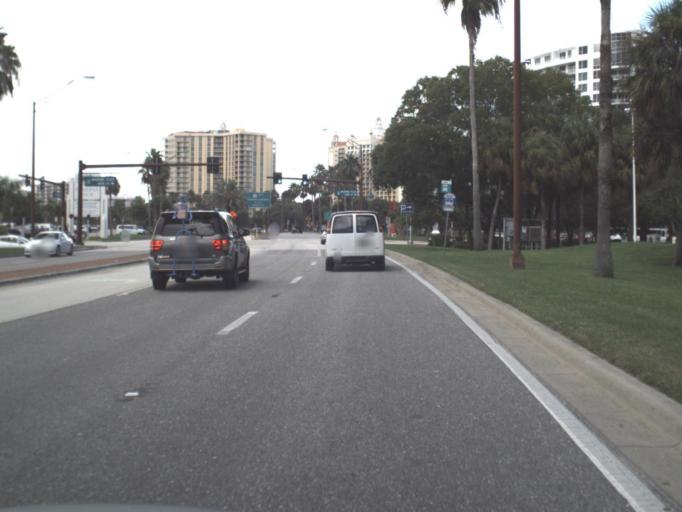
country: US
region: Florida
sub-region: Sarasota County
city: Sarasota
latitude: 27.3339
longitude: -82.5439
